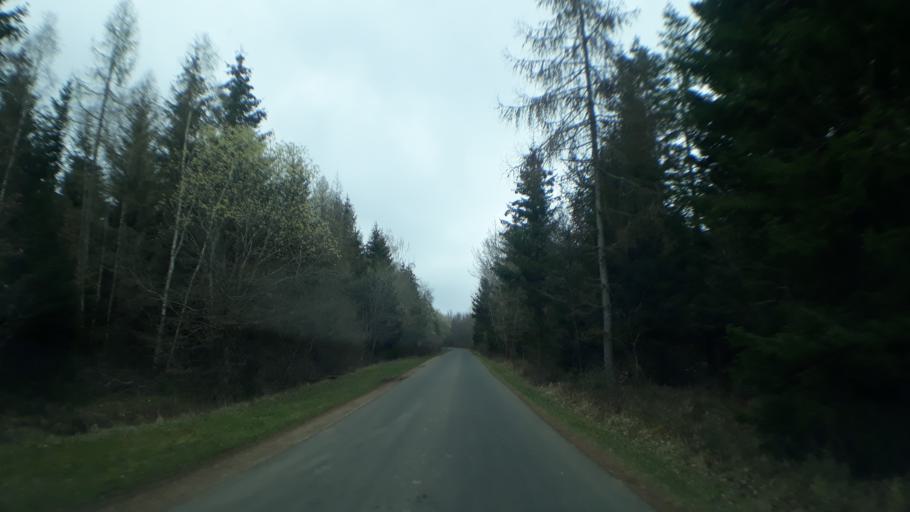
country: DE
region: North Rhine-Westphalia
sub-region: Regierungsbezirk Koln
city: Schleiden
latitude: 50.5283
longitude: 6.5109
